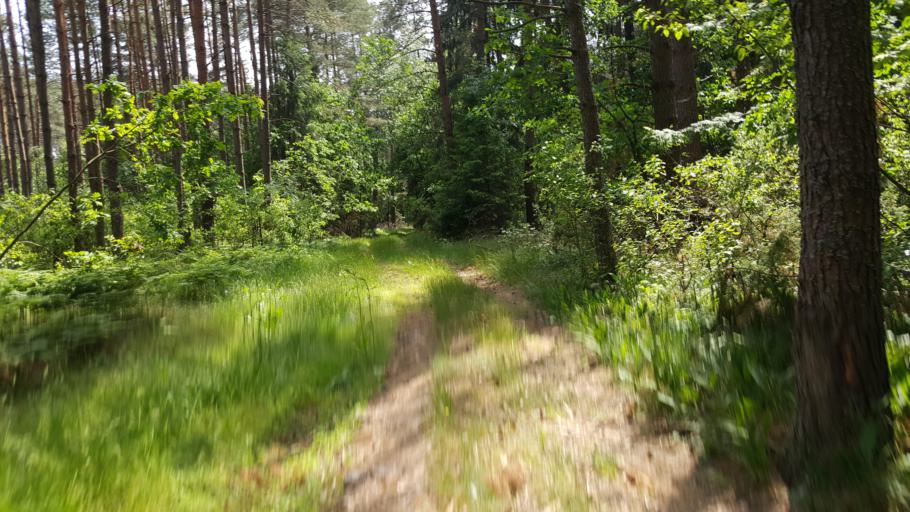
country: BY
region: Brest
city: Kamyanyuki
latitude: 52.5071
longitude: 23.8286
